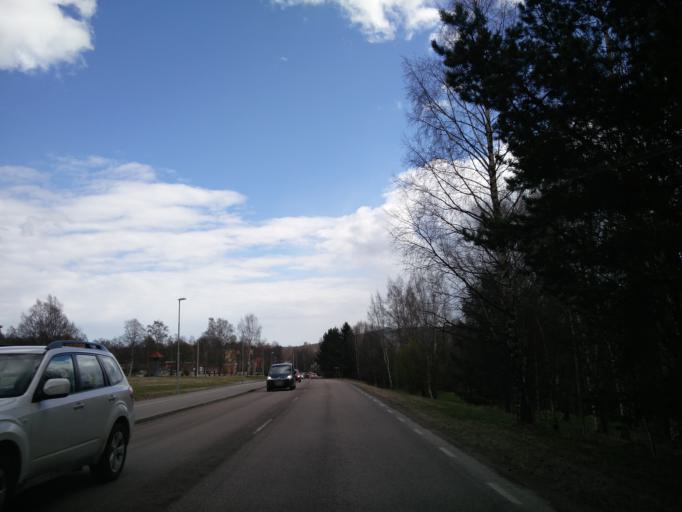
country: SE
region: Vaesternorrland
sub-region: Sundsvalls Kommun
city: Sundsvall
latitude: 62.4004
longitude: 17.2579
